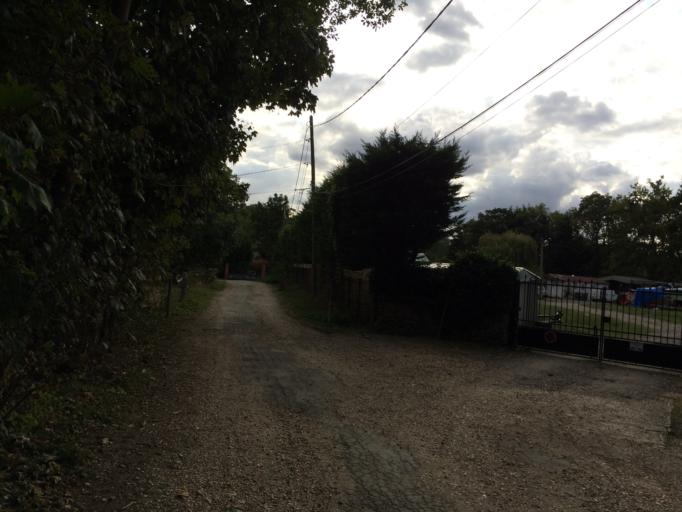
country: FR
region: Ile-de-France
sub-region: Departement de l'Essonne
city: Soisy-sur-Seine
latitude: 48.6524
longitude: 2.4349
